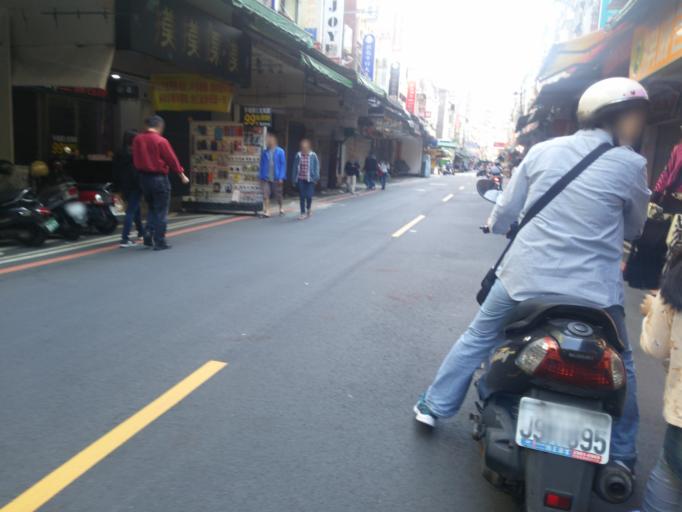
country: TW
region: Taipei
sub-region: Taipei
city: Banqiao
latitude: 24.9893
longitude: 121.5111
